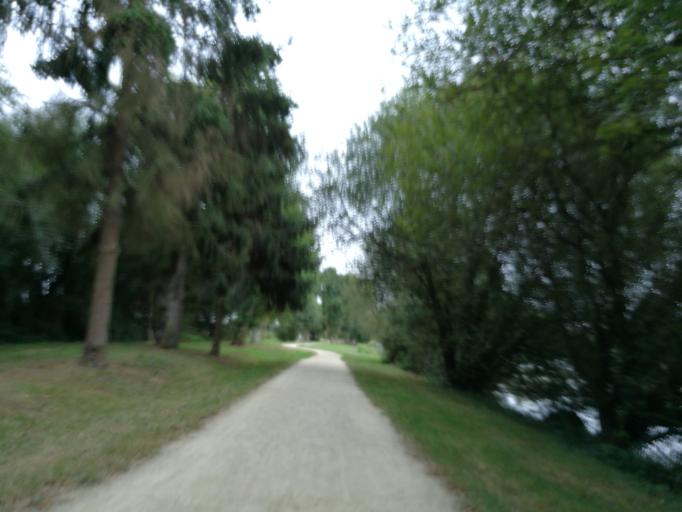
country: FR
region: Brittany
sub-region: Departement d'Ille-et-Vilaine
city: Bedee
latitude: 48.1687
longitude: -1.9532
